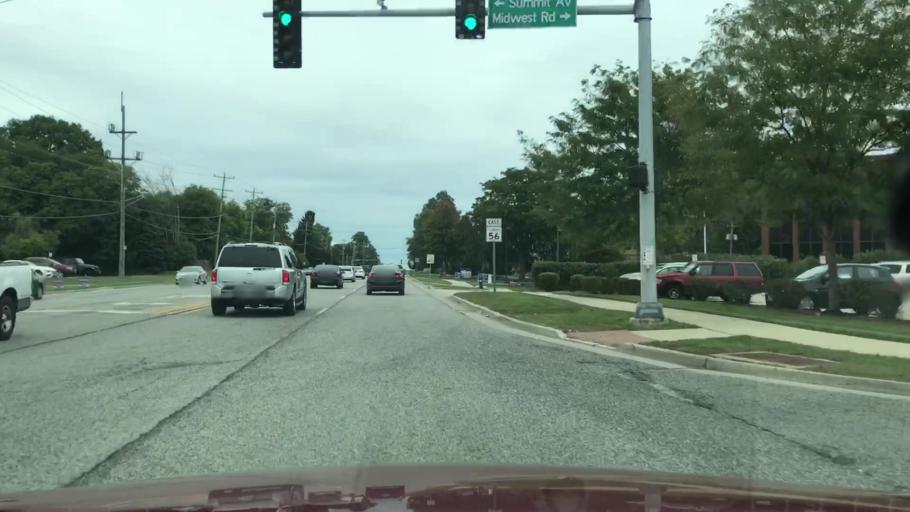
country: US
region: Illinois
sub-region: DuPage County
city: Oakbrook Terrace
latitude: 41.8511
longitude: -87.9724
